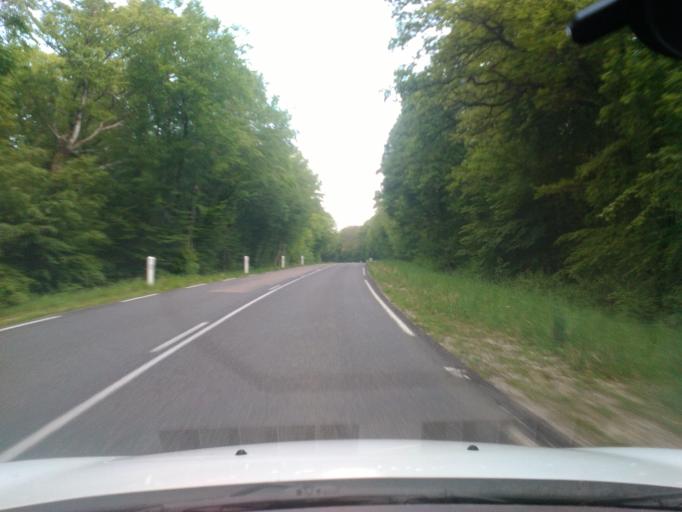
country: FR
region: Champagne-Ardenne
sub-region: Departement de la Haute-Marne
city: Lavilleneuve-au-Roi
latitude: 48.2067
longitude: 4.9330
